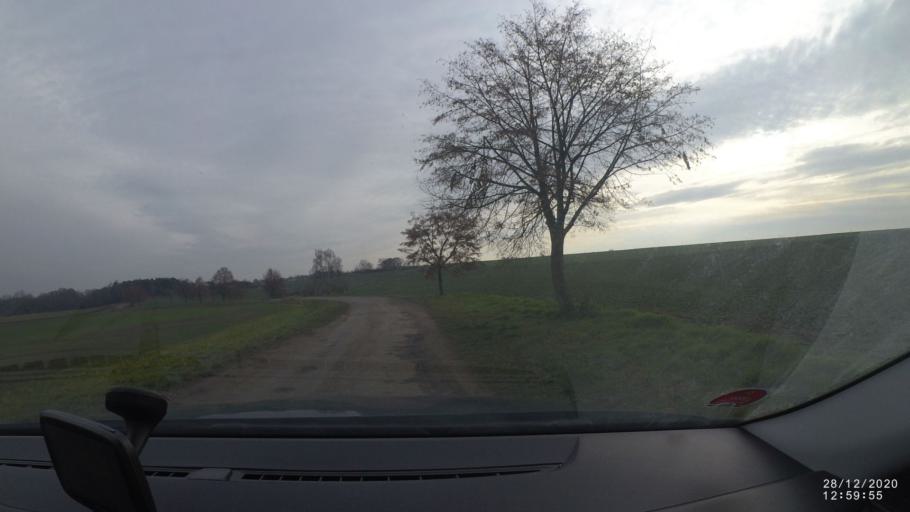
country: CZ
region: Praha
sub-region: Praha 19
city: Satalice
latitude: 50.1474
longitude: 14.5963
